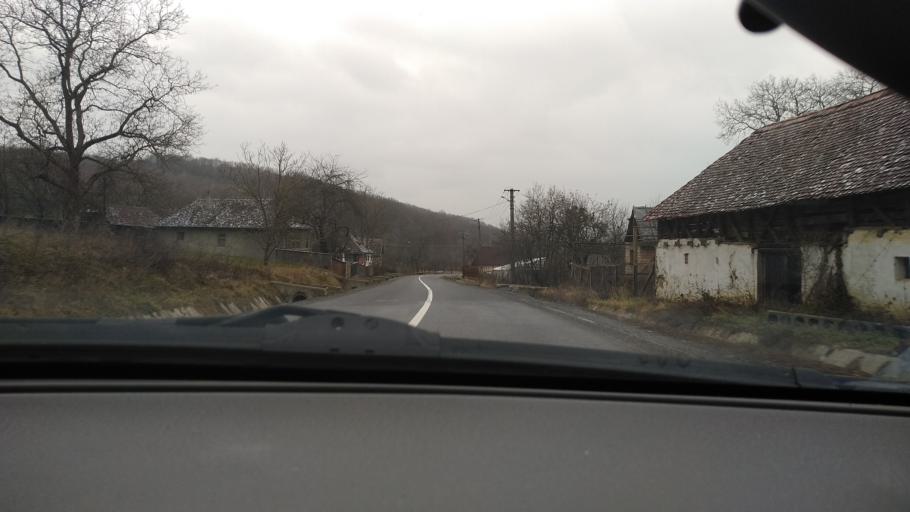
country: RO
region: Mures
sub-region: Comuna Magherani
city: Magherani
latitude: 46.5797
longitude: 24.9354
